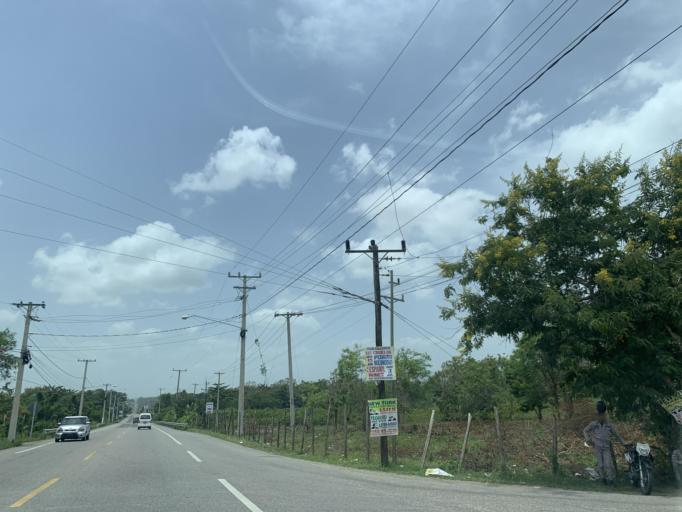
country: DO
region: Puerto Plata
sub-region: Puerto Plata
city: Puerto Plata
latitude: 19.7533
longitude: -70.6418
